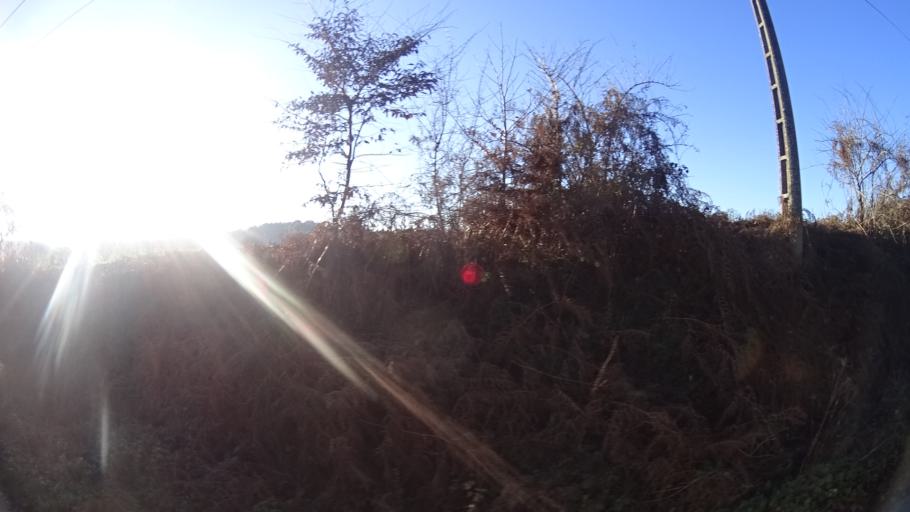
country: FR
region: Brittany
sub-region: Departement du Morbihan
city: Saint-Jacut-les-Pins
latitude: 47.6729
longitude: -2.1816
